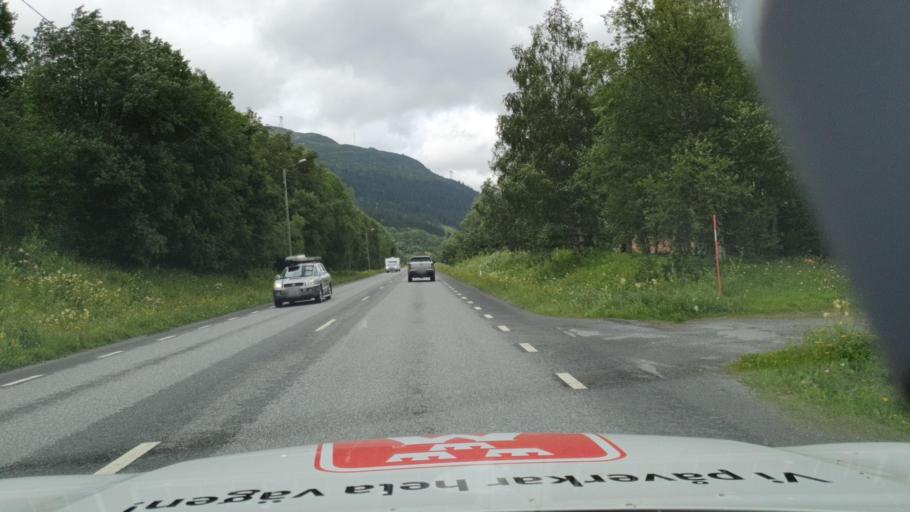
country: SE
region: Jaemtland
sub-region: Are Kommun
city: Are
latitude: 63.4051
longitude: 13.0281
